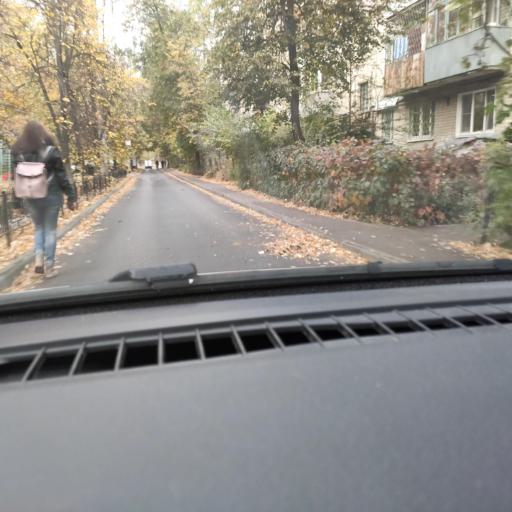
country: RU
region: Voronezj
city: Pridonskoy
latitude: 51.6477
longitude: 39.1248
